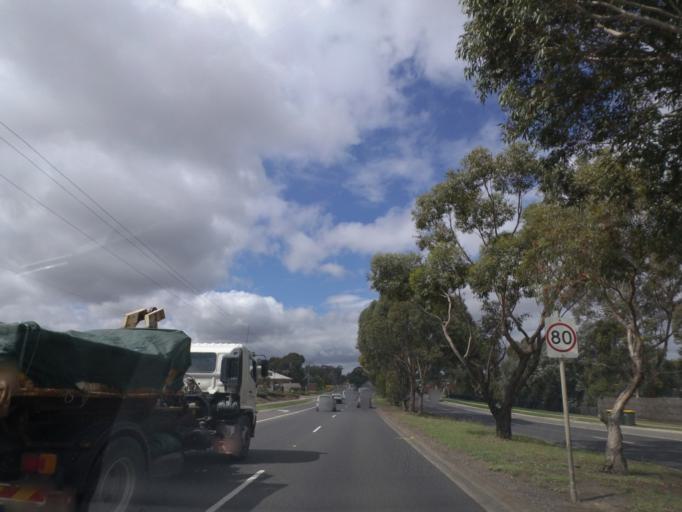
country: AU
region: Victoria
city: Plenty
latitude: -37.6815
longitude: 145.1210
